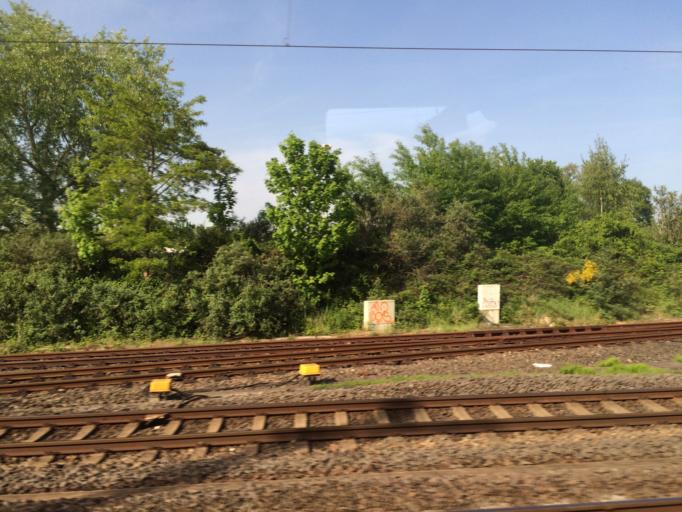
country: DE
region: North Rhine-Westphalia
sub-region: Regierungsbezirk Koln
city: Troisdorf
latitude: 50.8183
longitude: 7.1370
